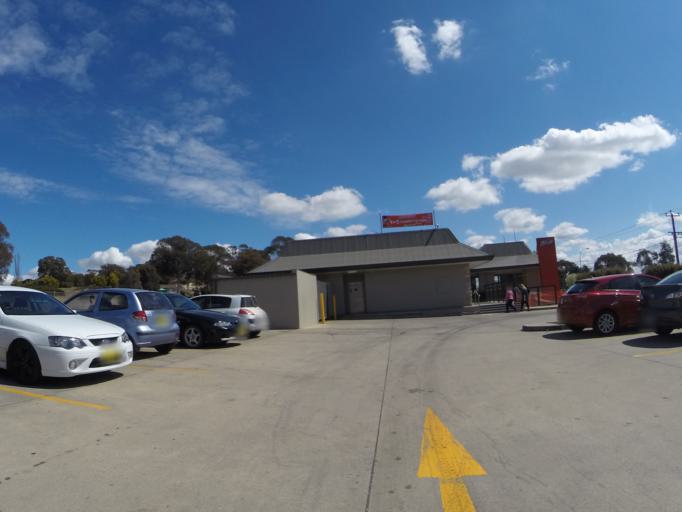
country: AU
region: New South Wales
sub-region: Goulburn Mulwaree
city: Goulburn
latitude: -34.7478
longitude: 149.7481
